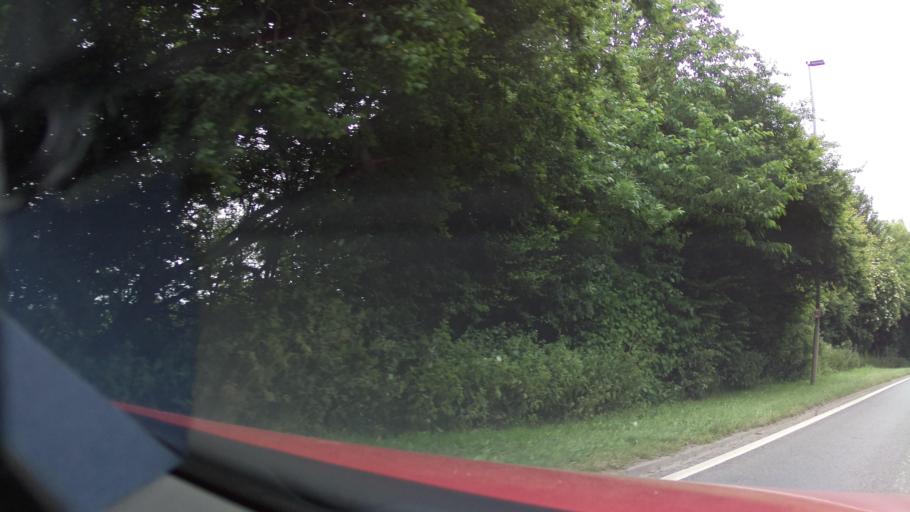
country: GB
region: England
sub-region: Leicestershire
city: Coalville
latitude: 52.7301
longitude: -1.3644
